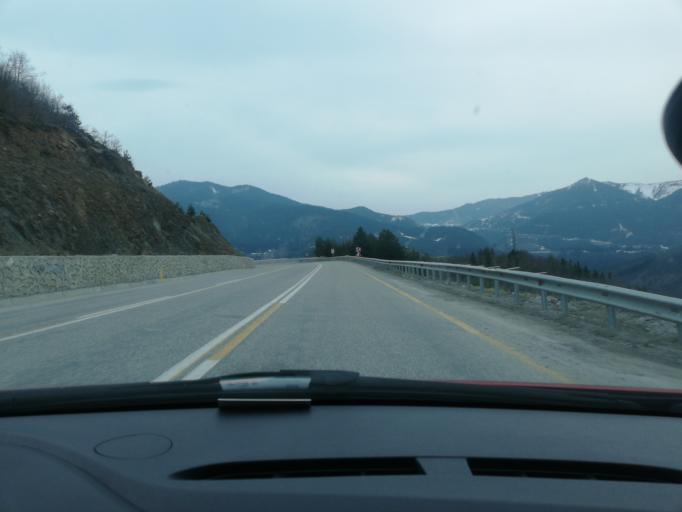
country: TR
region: Kastamonu
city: Kure
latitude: 41.8503
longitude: 33.7138
